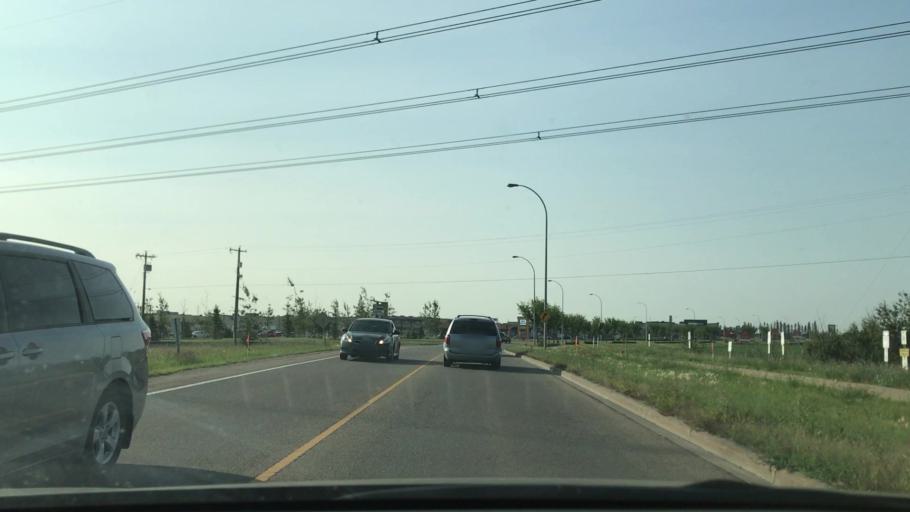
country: CA
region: Alberta
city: Beaumont
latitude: 53.4330
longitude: -113.4814
